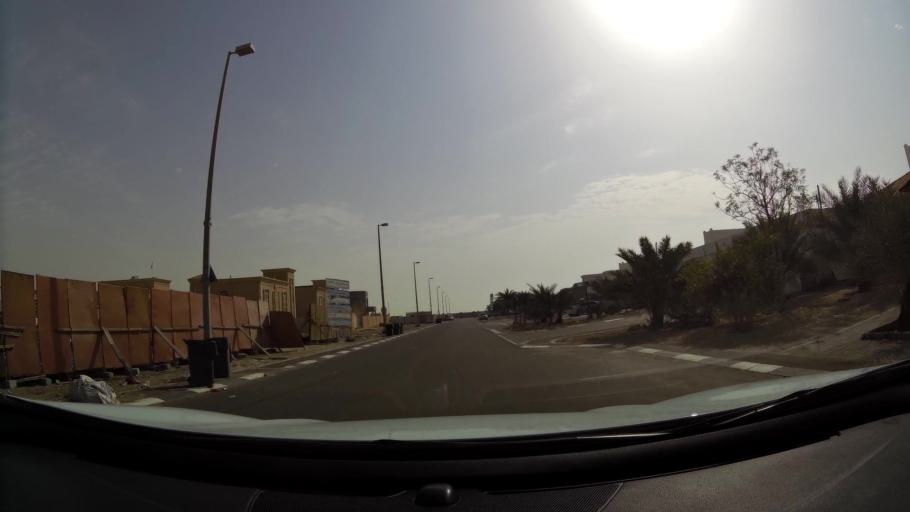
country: AE
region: Abu Dhabi
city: Abu Dhabi
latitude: 24.2770
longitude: 54.6932
